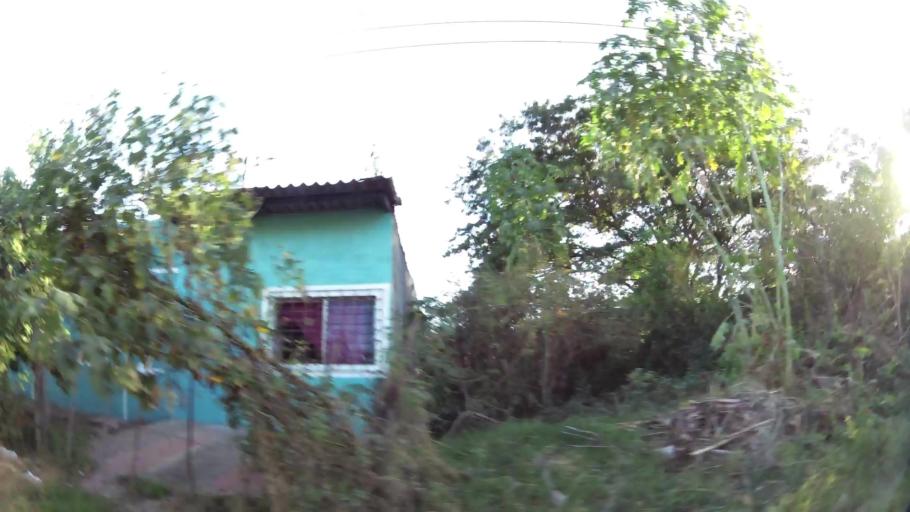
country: SV
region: San Miguel
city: San Miguel
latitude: 13.4629
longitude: -88.1694
